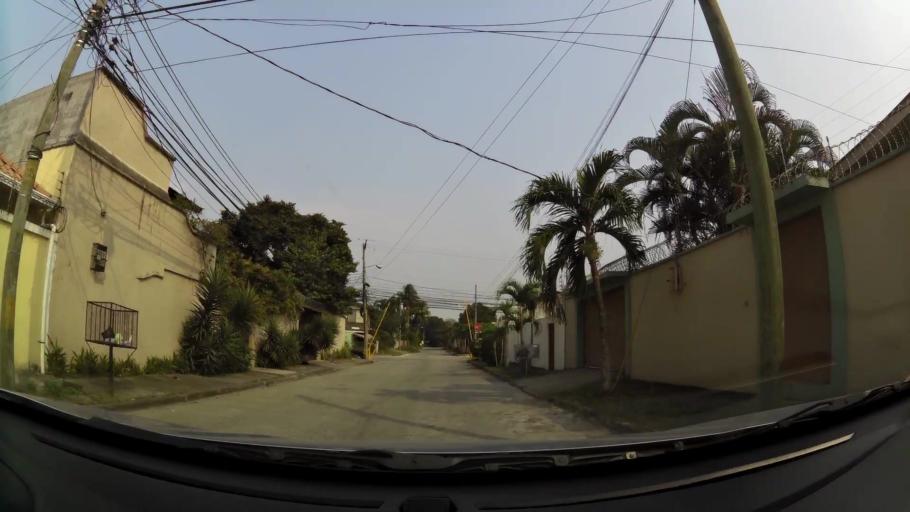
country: HN
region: Cortes
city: El Zapotal del Norte
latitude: 15.5170
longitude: -88.0380
